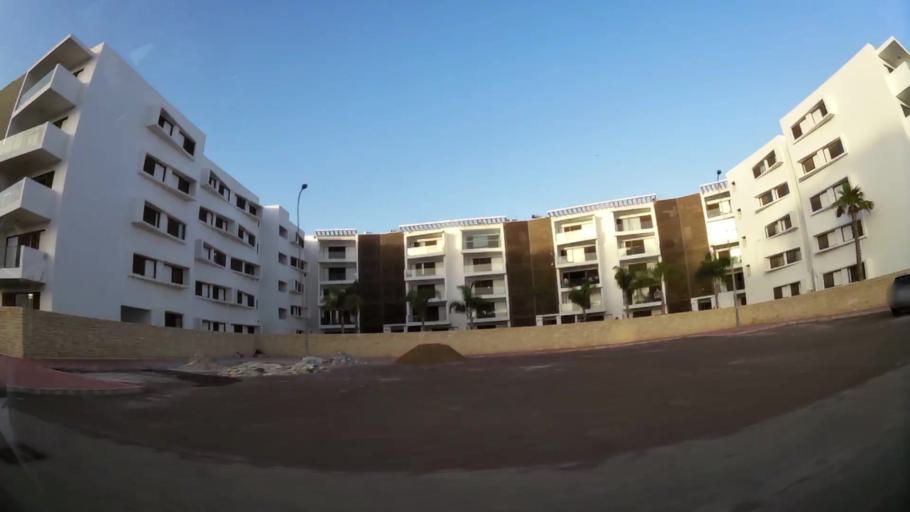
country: MA
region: Souss-Massa-Draa
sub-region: Agadir-Ida-ou-Tnan
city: Agadir
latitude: 30.3989
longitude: -9.5896
